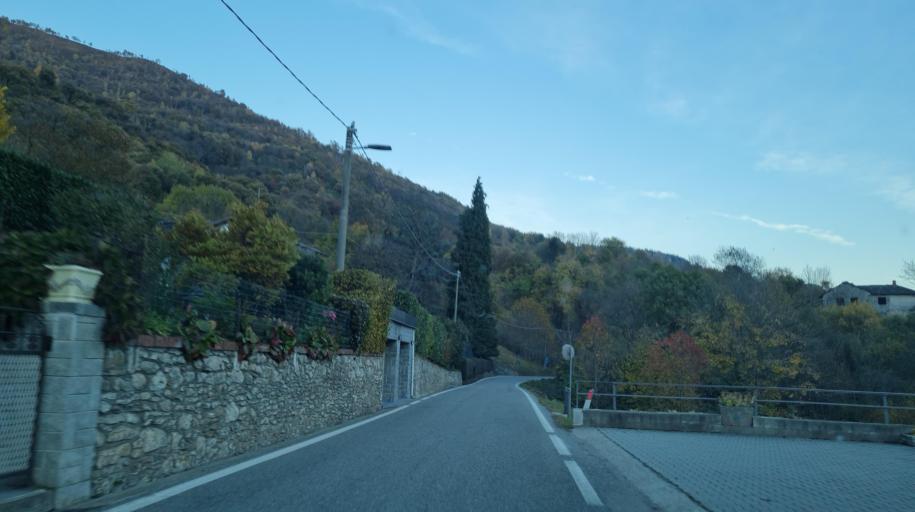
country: IT
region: Piedmont
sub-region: Provincia di Torino
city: Trausella
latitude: 45.4989
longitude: 7.7642
